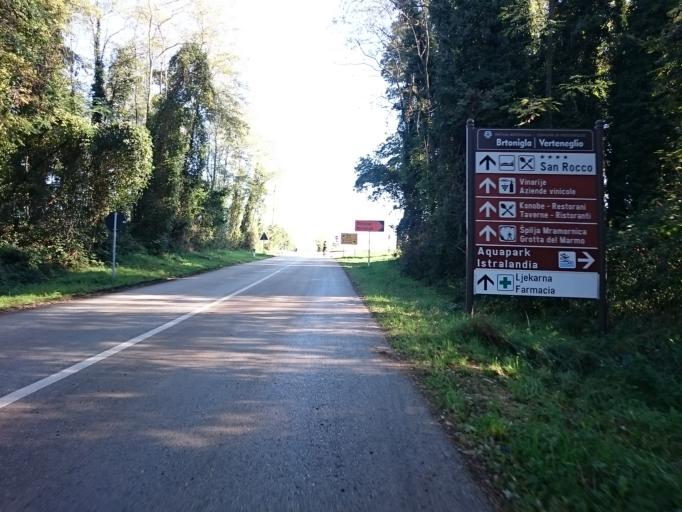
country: HR
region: Istarska
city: Buje
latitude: 45.3662
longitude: 13.6085
